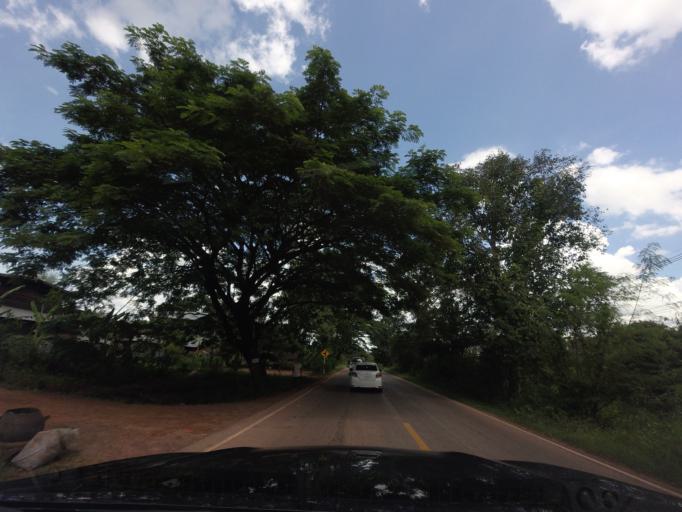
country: TH
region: Changwat Udon Thani
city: Ban Dung
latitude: 17.6542
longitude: 103.1398
